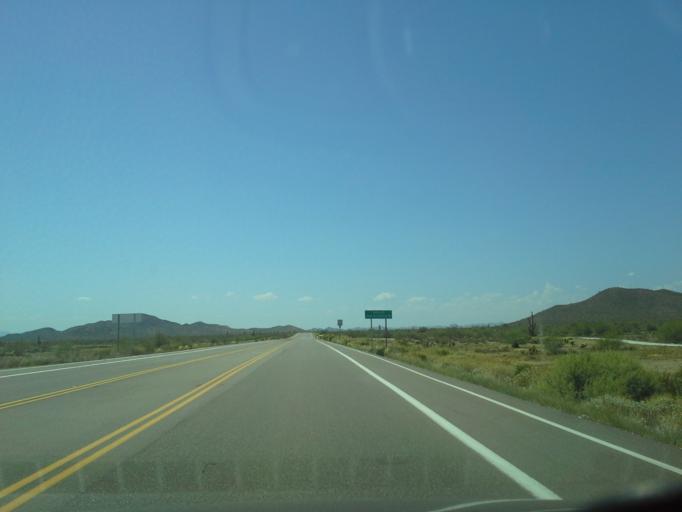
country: US
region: Arizona
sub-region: Maricopa County
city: Cave Creek
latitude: 33.7631
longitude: -112.0297
